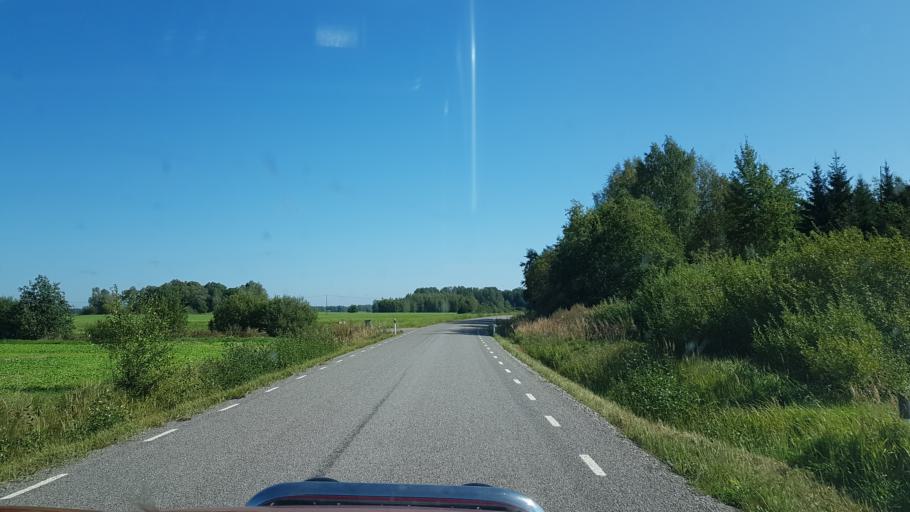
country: EE
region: Polvamaa
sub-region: Polva linn
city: Polva
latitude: 58.2176
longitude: 27.2063
